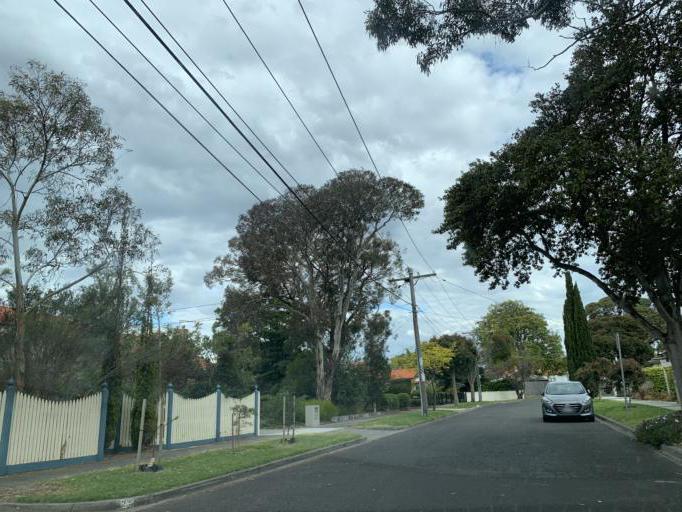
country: AU
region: Victoria
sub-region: Bayside
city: Hampton
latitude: -37.9327
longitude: 145.0081
